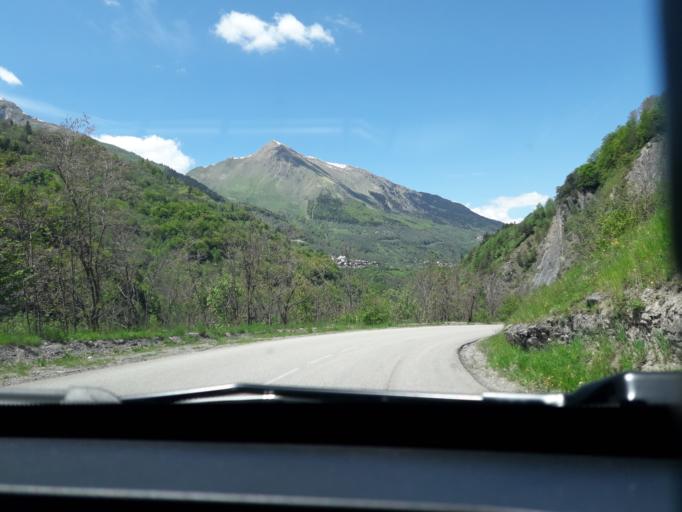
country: FR
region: Rhone-Alpes
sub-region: Departement de la Savoie
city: Saint-Martin-de-Belleville
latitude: 45.4076
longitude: 6.4910
